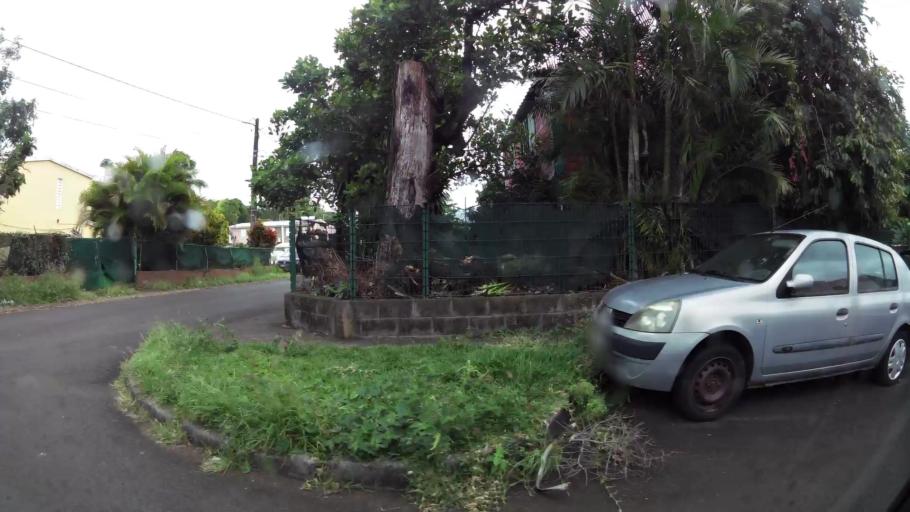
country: RE
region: Reunion
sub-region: Reunion
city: Sainte-Marie
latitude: -20.9015
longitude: 55.5497
